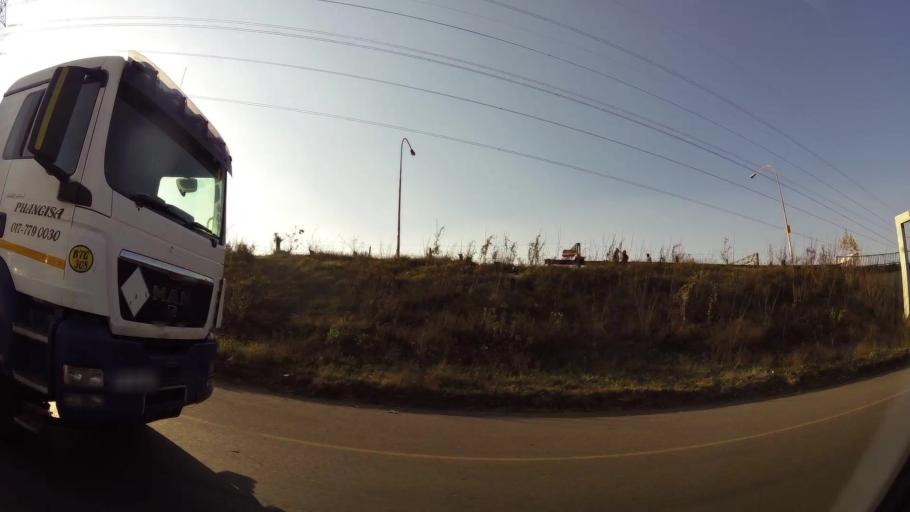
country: ZA
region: Gauteng
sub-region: Ekurhuleni Metropolitan Municipality
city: Germiston
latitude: -26.2101
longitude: 28.1225
